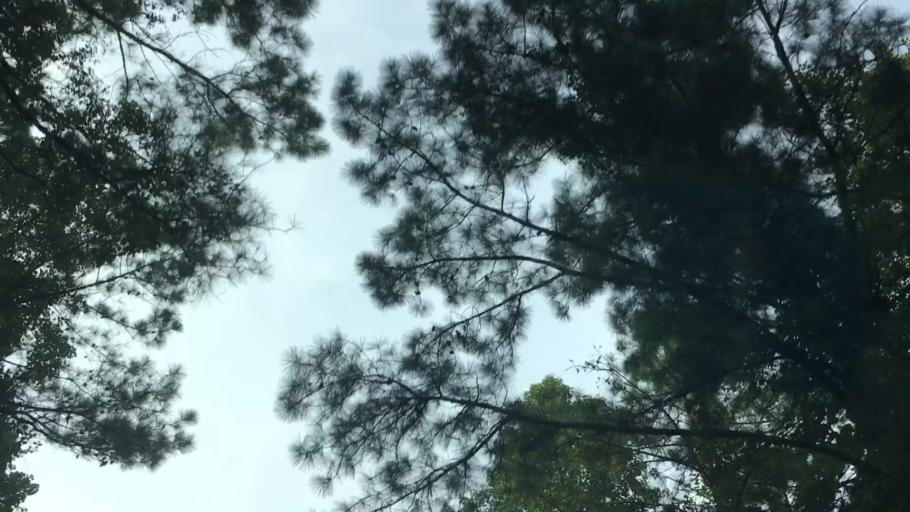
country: US
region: Alabama
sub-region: Bibb County
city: Woodstock
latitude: 33.2341
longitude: -87.1441
